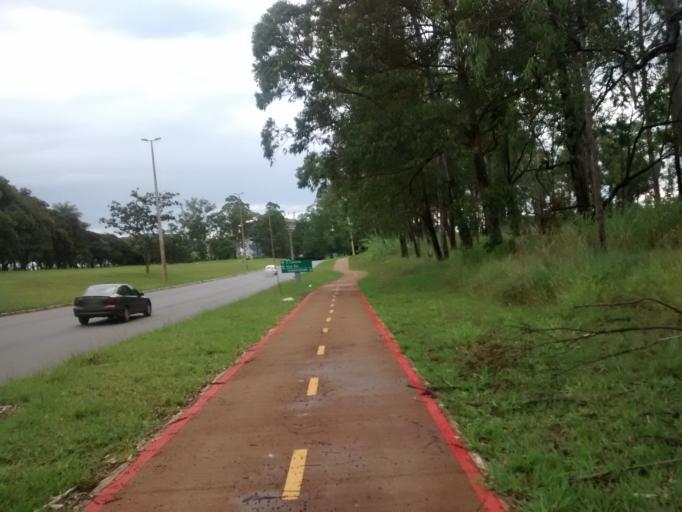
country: BR
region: Federal District
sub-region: Brasilia
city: Brasilia
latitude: -15.7787
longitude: -47.8686
